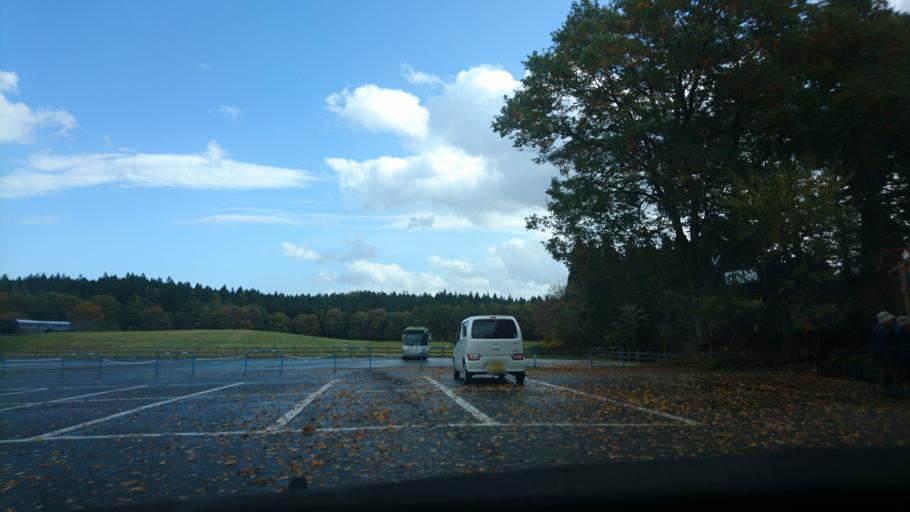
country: JP
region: Iwate
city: Shizukuishi
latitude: 39.7494
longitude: 141.0168
